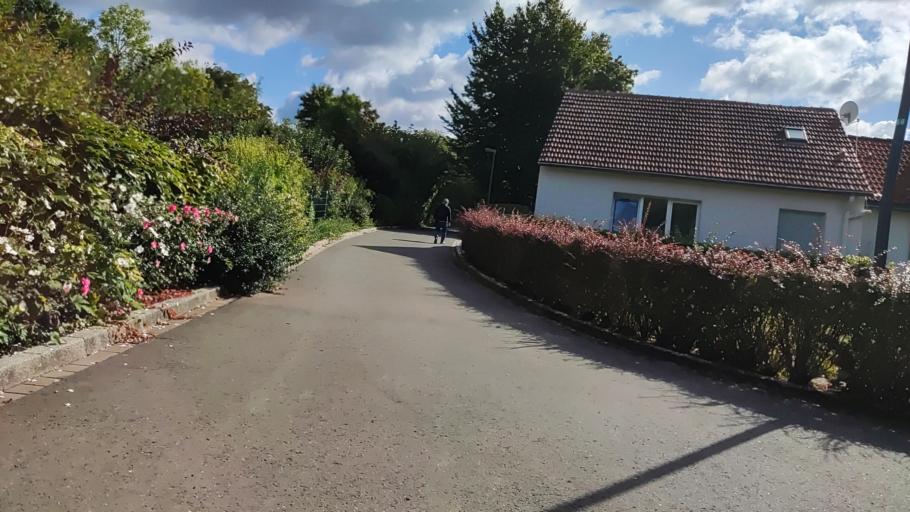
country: DE
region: North Rhine-Westphalia
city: Bochum-Hordel
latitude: 51.5217
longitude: 7.1752
